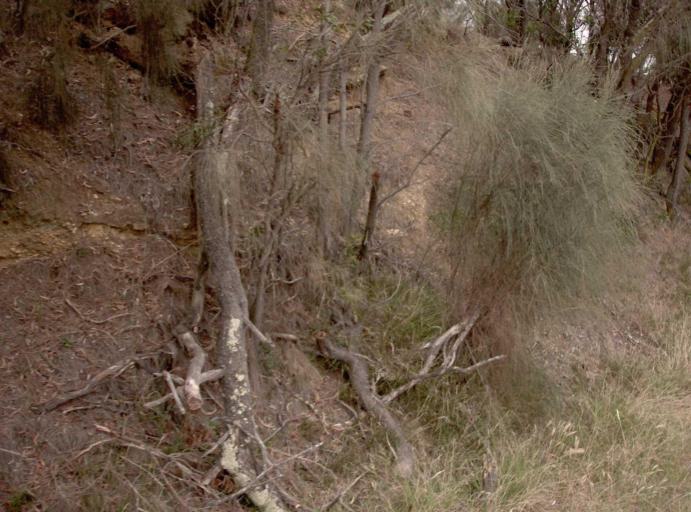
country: AU
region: Victoria
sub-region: Wellington
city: Heyfield
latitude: -38.1257
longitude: 146.7836
